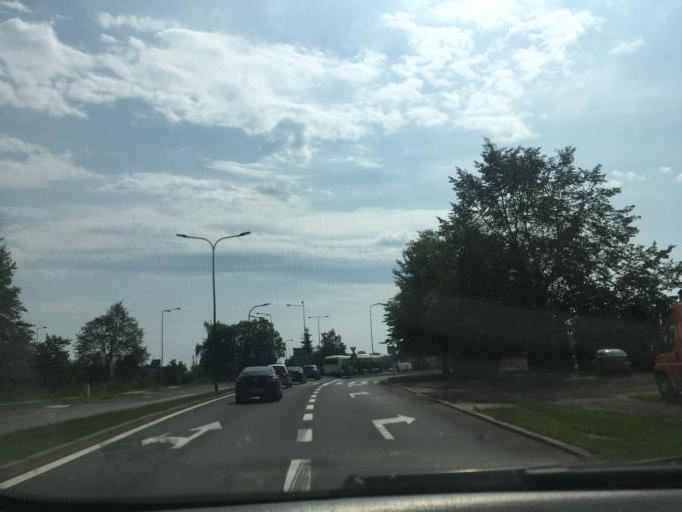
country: PL
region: Silesian Voivodeship
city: Zebrzydowice
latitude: 50.0927
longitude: 18.5179
